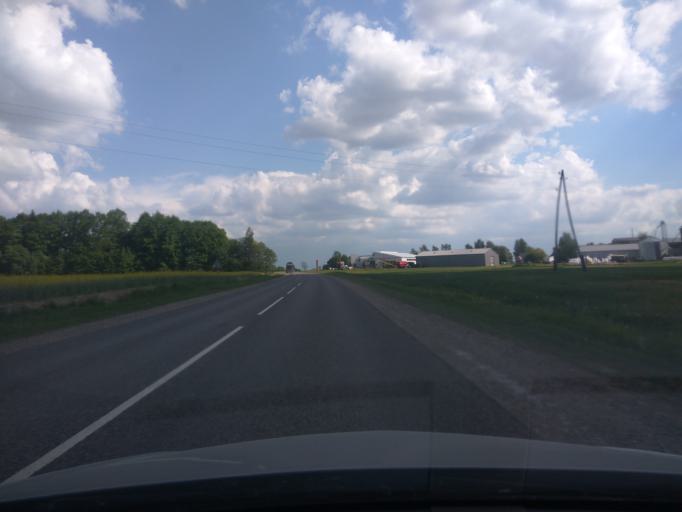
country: LV
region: Kuldigas Rajons
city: Kuldiga
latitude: 57.0007
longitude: 21.8973
